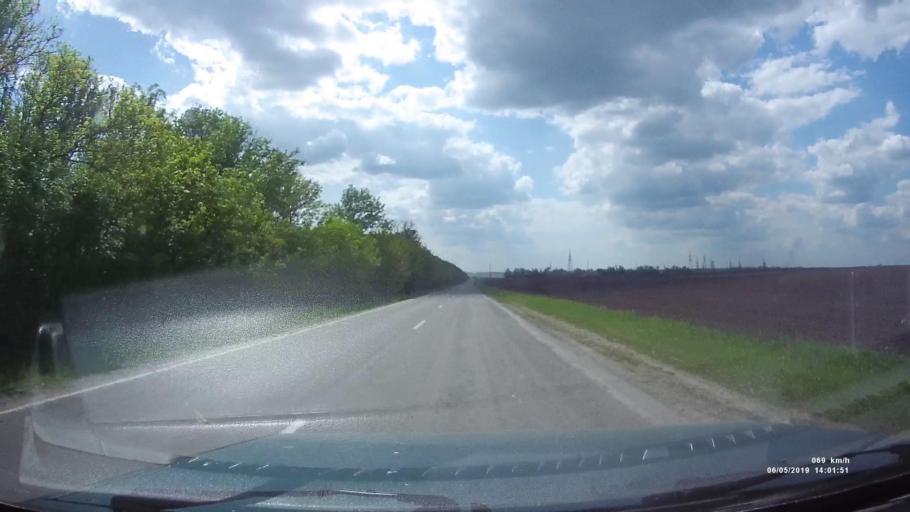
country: RU
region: Rostov
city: Shakhty
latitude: 47.6838
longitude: 40.3728
